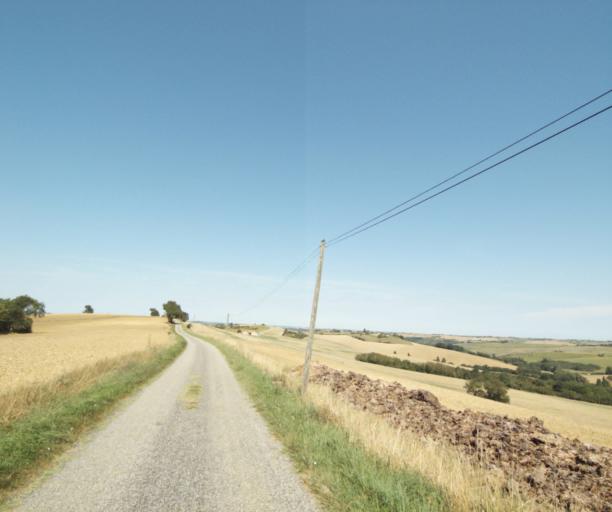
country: FR
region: Midi-Pyrenees
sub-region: Departement de l'Ariege
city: Lezat-sur-Leze
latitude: 43.2620
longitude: 1.3863
